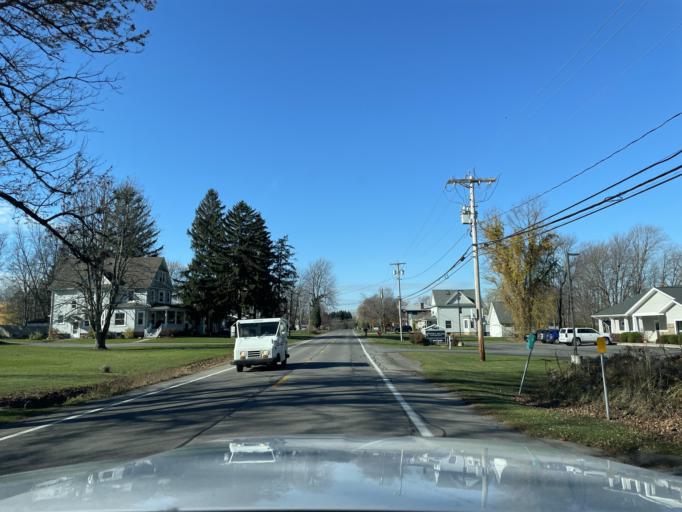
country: US
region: New York
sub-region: Orleans County
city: Medina
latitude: 43.2210
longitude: -78.4079
